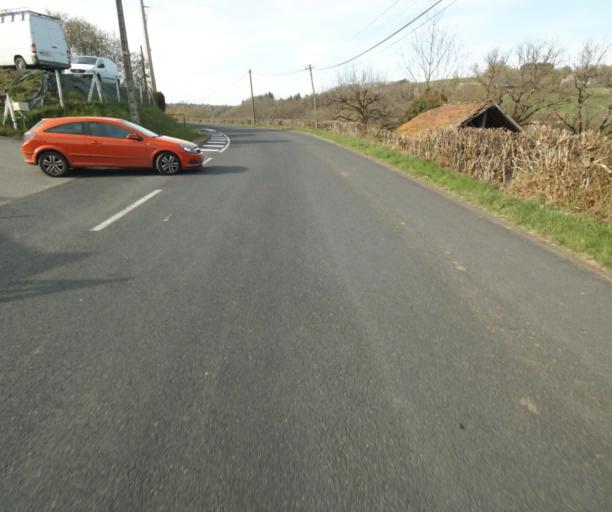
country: FR
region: Limousin
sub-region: Departement de la Correze
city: Tulle
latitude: 45.2871
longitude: 1.7606
